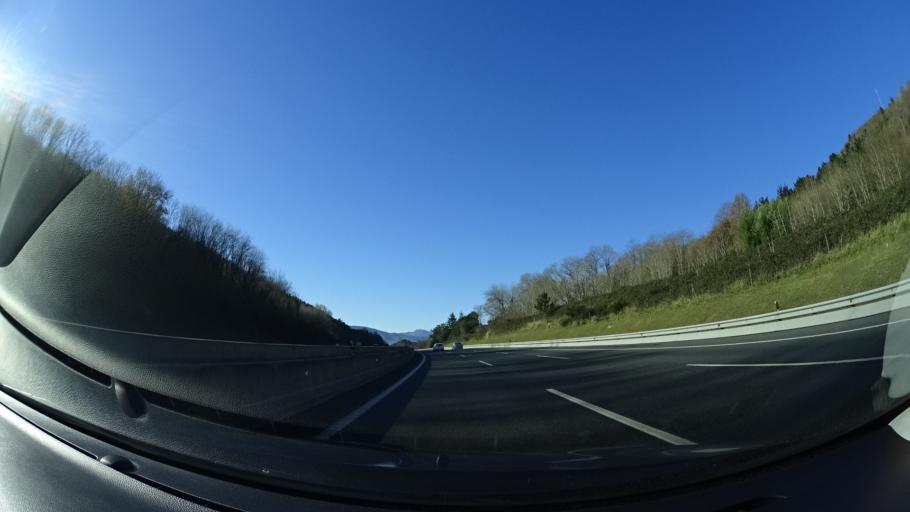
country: ES
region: Basque Country
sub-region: Provincia de Guipuzcoa
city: Usurbil
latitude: 43.2952
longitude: -2.0617
